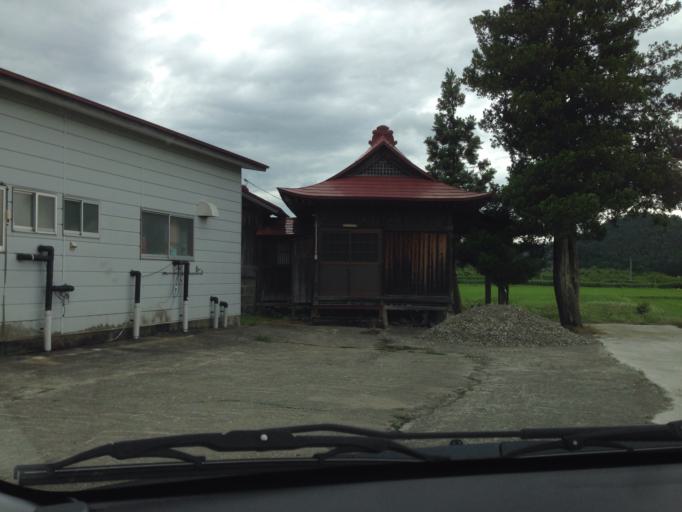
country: JP
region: Fukushima
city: Kitakata
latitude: 37.4393
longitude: 139.9154
